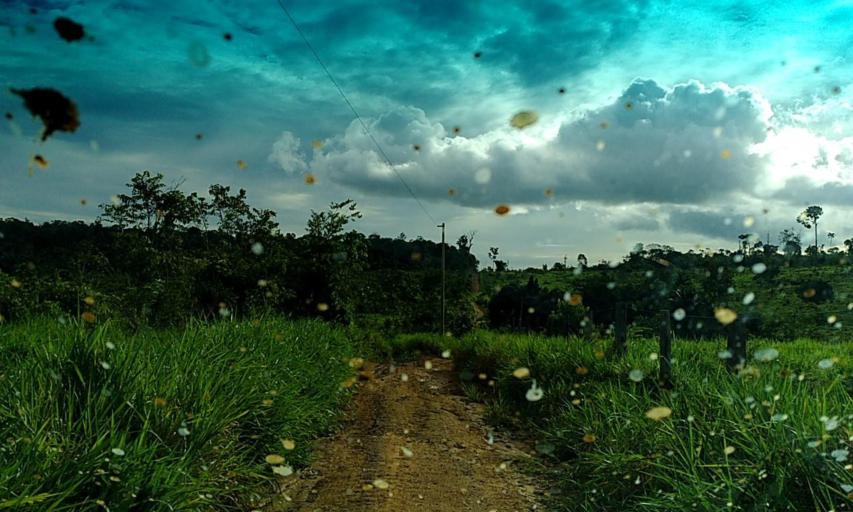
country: BR
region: Para
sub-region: Senador Jose Porfirio
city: Senador Jose Porfirio
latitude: -3.0035
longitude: -51.7398
